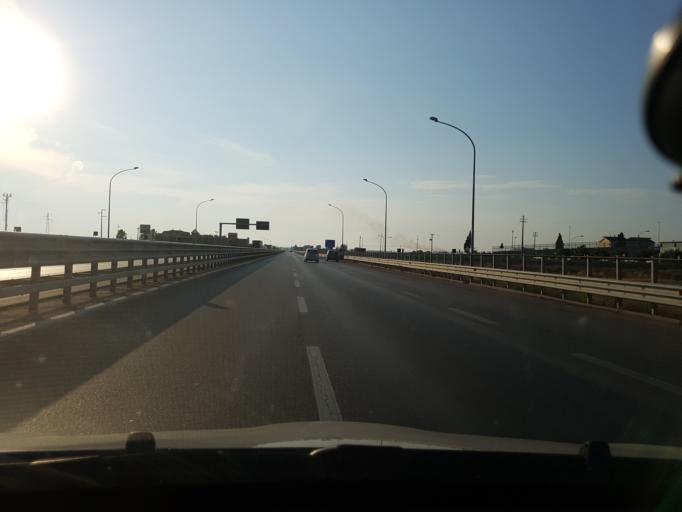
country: IT
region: Apulia
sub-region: Provincia di Foggia
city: Orta Nova
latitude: 41.3465
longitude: 15.7347
